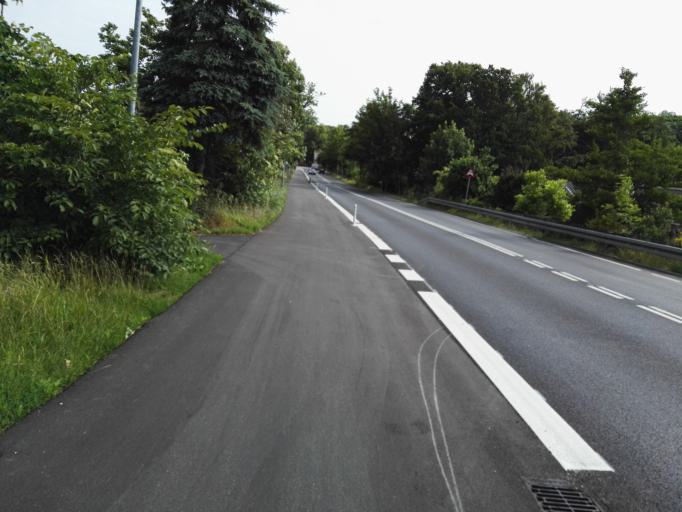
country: DK
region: Zealand
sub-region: Roskilde Kommune
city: Jyllinge
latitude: 55.7640
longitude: 12.1183
